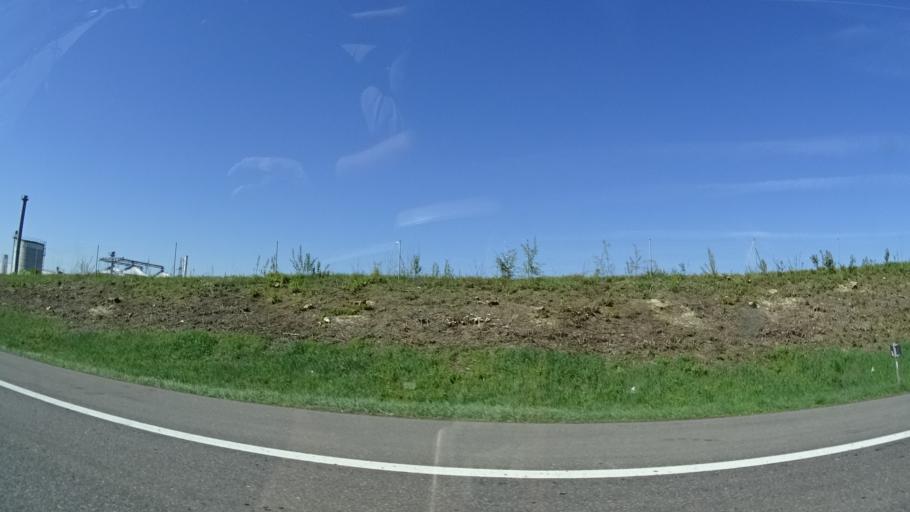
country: DE
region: Baden-Wuerttemberg
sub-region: Karlsruhe Region
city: Empfingen
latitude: 48.3966
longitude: 8.7292
